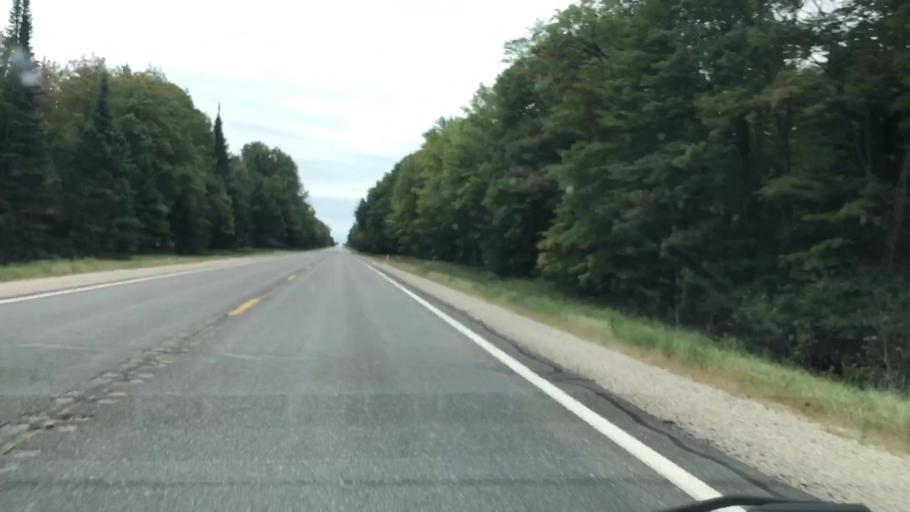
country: US
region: Michigan
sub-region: Luce County
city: Newberry
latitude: 46.2294
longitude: -85.5721
